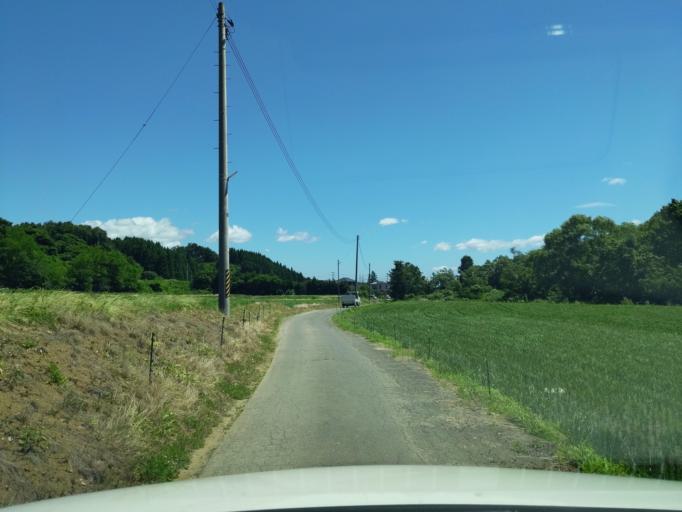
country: JP
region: Fukushima
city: Koriyama
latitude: 37.3959
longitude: 140.2522
